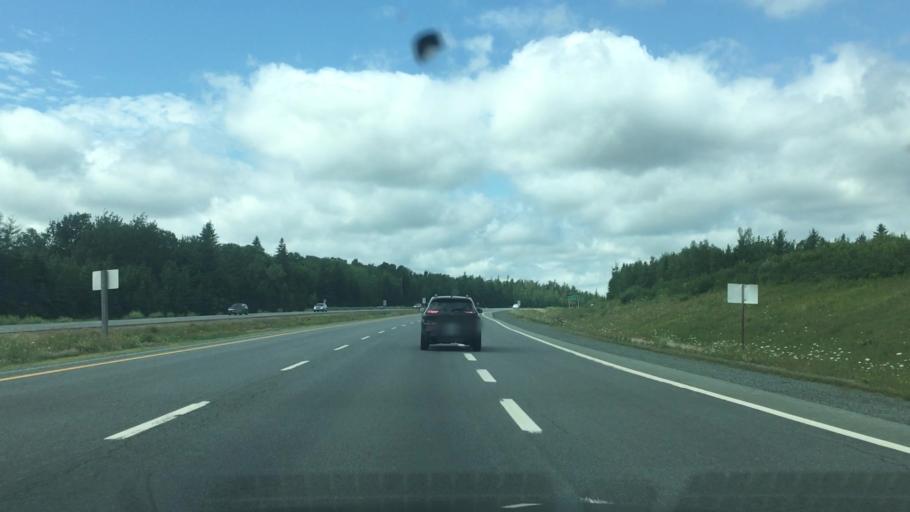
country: CA
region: Nova Scotia
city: Springhill
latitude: 45.6923
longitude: -64.0091
